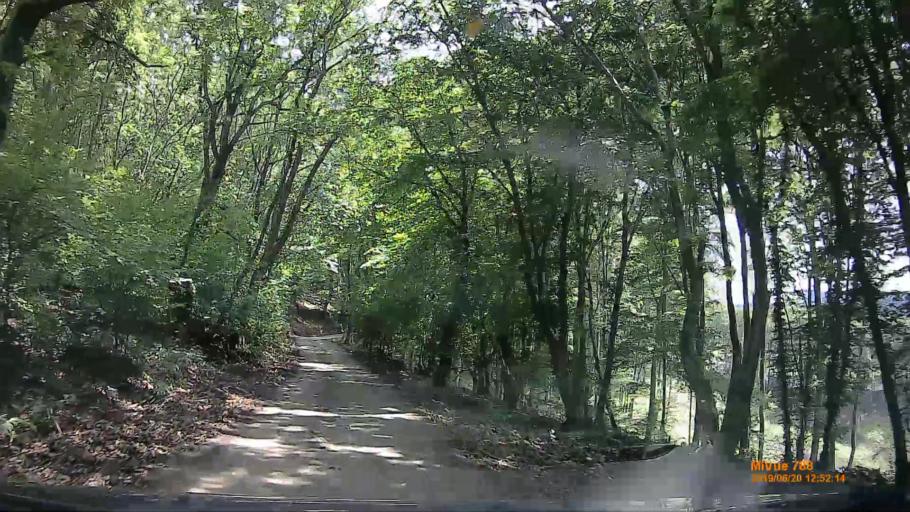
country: HU
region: Baranya
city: Hosszuheteny
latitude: 46.2145
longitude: 18.3597
